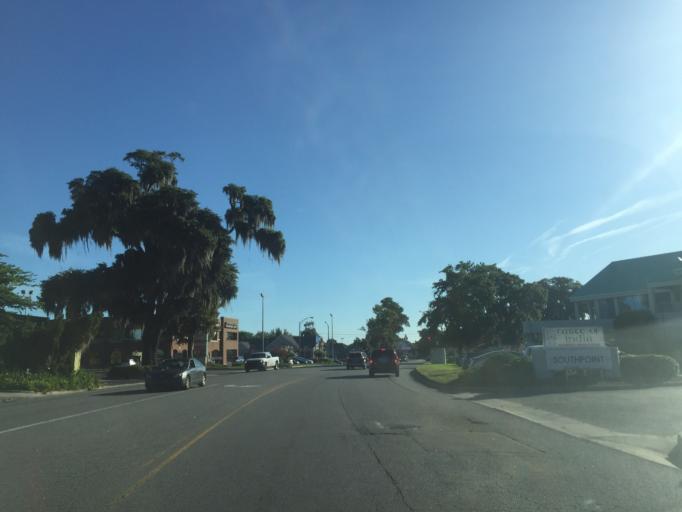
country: US
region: Georgia
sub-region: Chatham County
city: Isle of Hope
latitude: 32.0018
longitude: -81.1131
